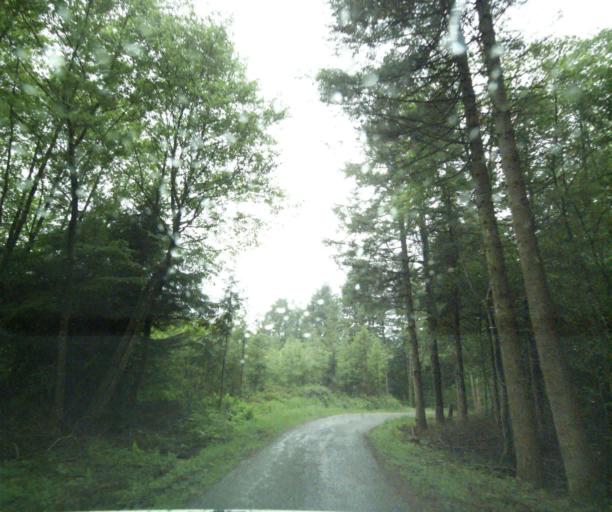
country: FR
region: Bourgogne
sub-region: Departement de Saone-et-Loire
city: Charolles
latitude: 46.3741
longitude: 4.3637
